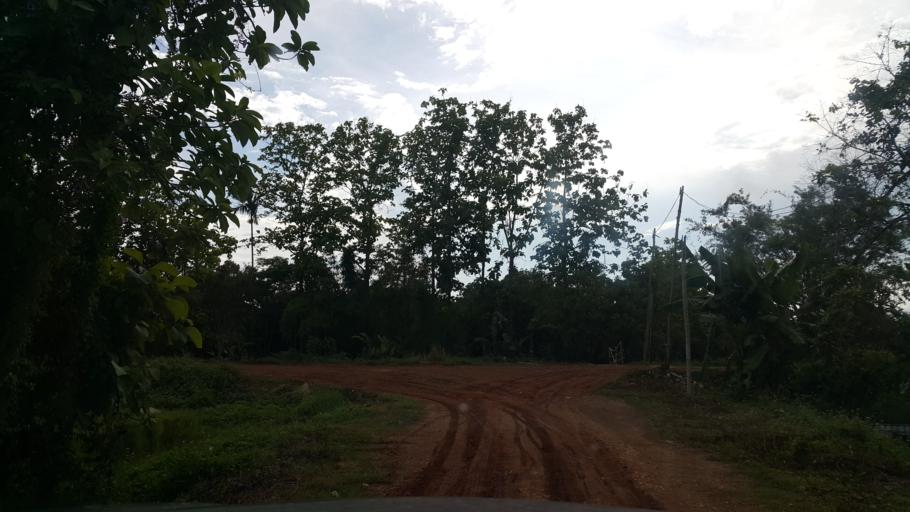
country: TH
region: Chiang Rai
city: Wiang Chai
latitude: 19.9749
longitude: 99.9071
